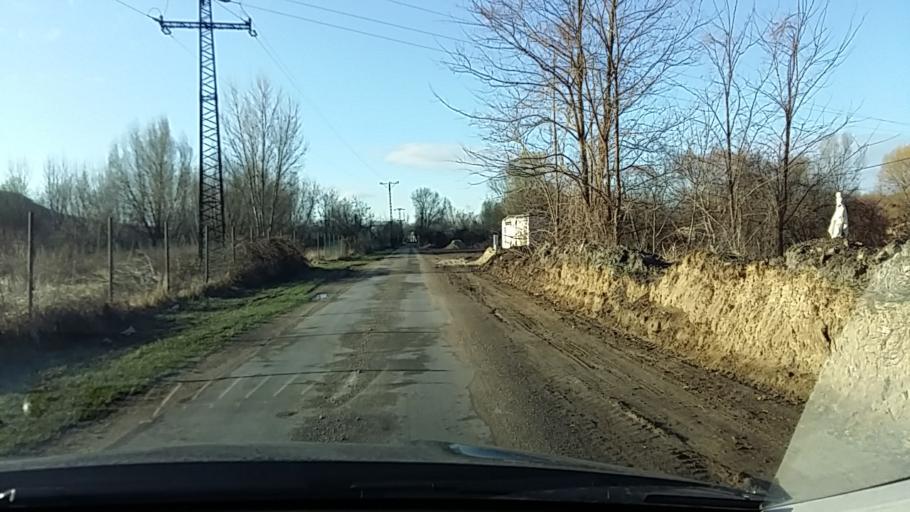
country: HU
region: Veszprem
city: Tapolca
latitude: 46.8762
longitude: 17.4391
